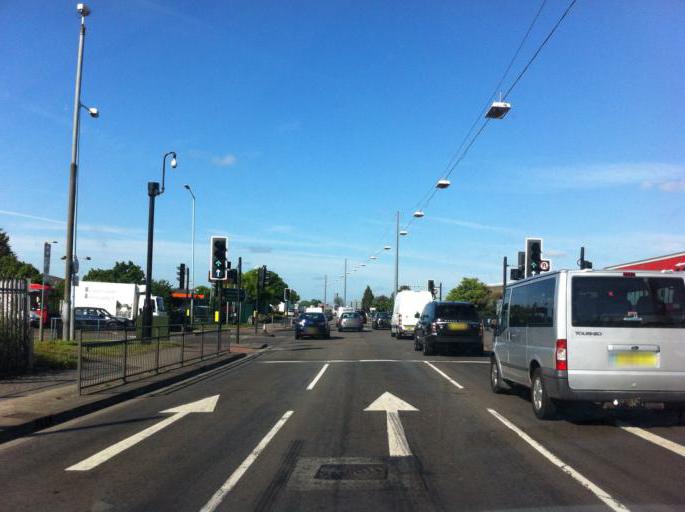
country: GB
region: England
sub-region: Greater London
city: Feltham
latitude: 51.4667
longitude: -0.4216
